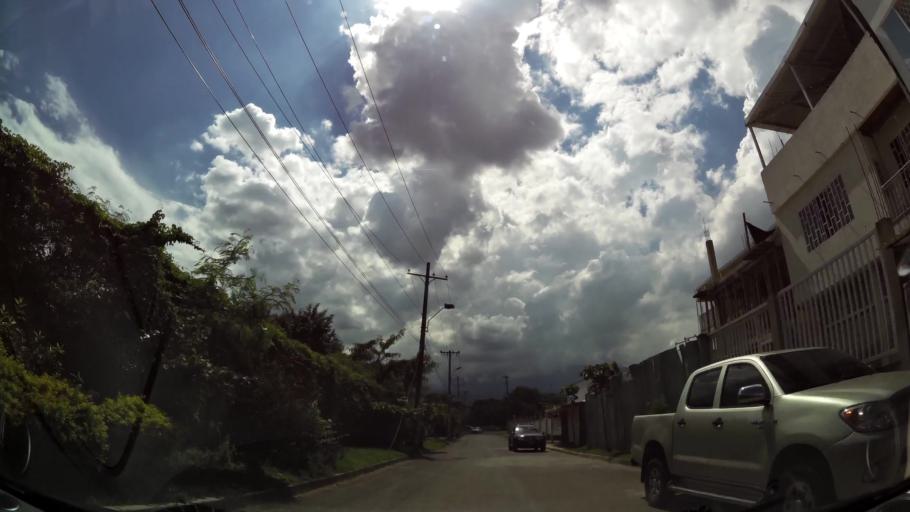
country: CO
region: Valle del Cauca
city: Cali
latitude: 3.4004
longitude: -76.5219
